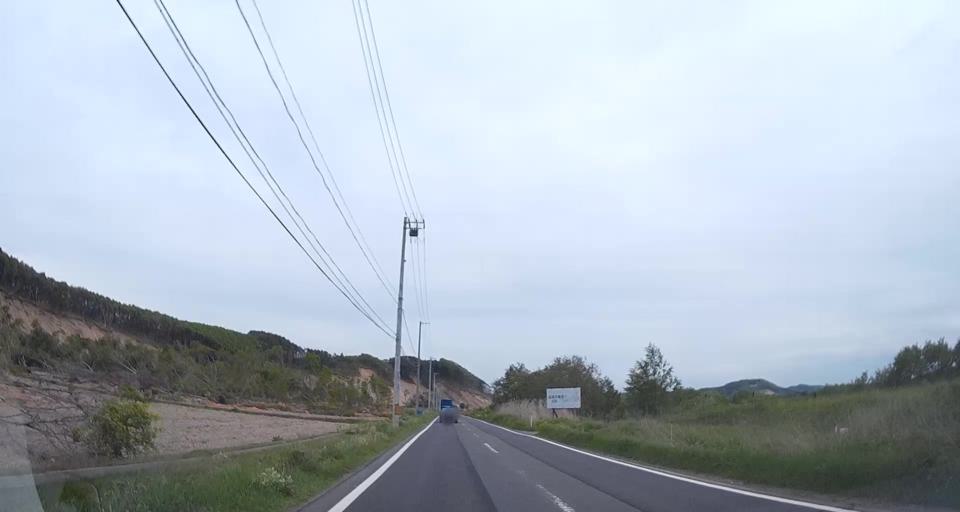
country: JP
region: Hokkaido
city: Chitose
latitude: 42.7445
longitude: 141.9067
